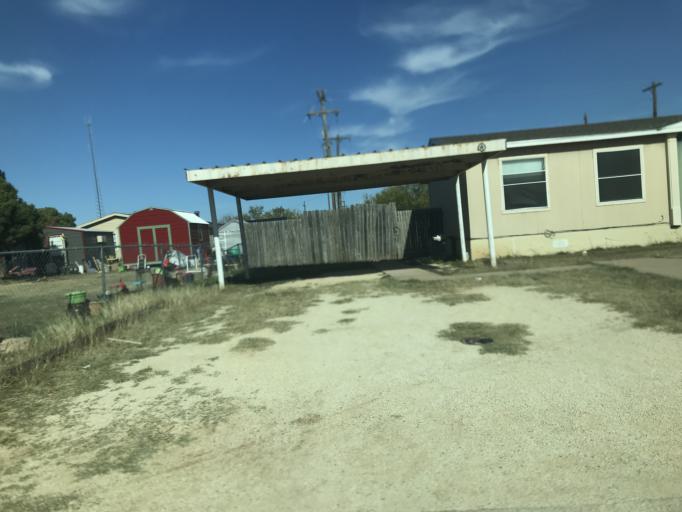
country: US
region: Texas
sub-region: Taylor County
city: Abilene
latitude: 32.5008
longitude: -99.7593
